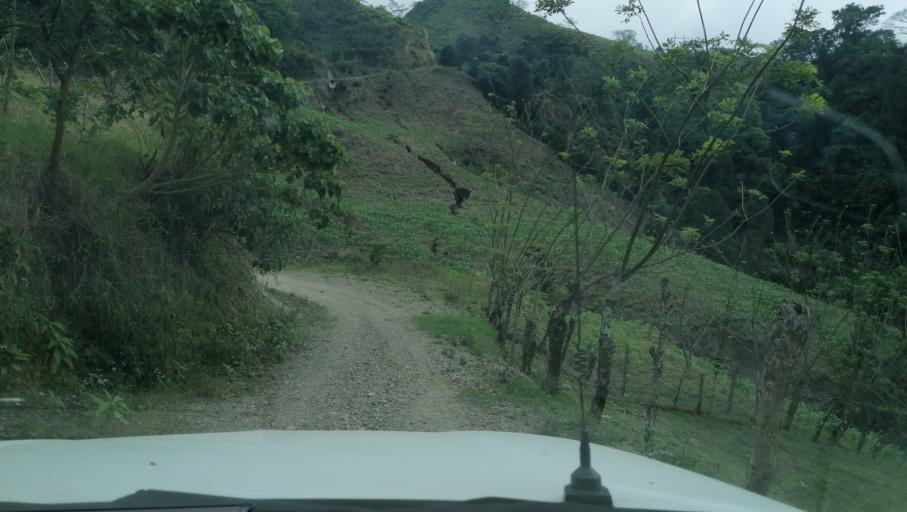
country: MX
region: Chiapas
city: Ostuacan
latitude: 17.3493
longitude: -93.3092
